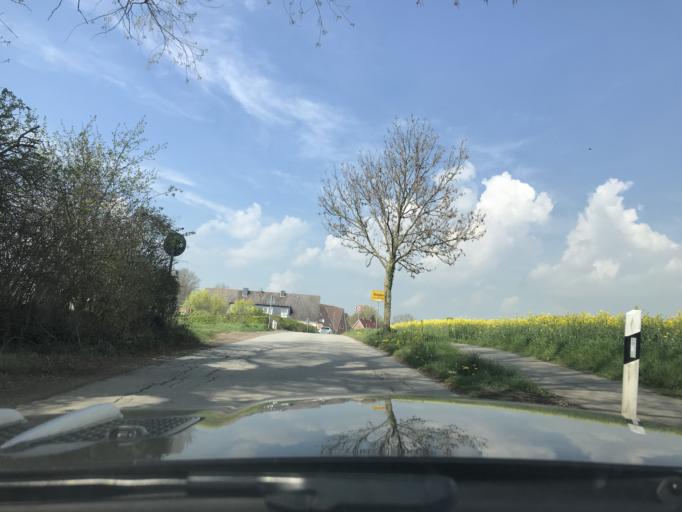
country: DE
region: Schleswig-Holstein
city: Schashagen
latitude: 54.1280
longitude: 10.9168
